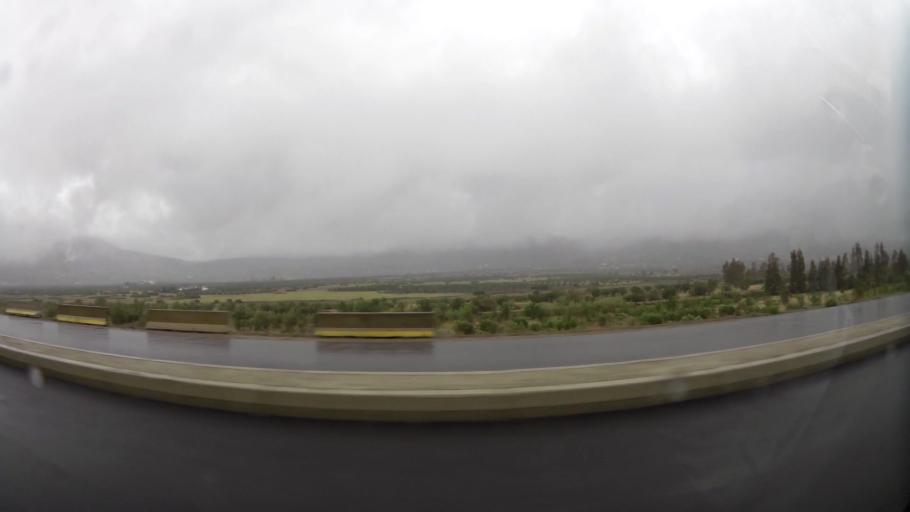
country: MA
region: Oriental
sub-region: Nador
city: Midar
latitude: 34.8274
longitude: -3.7203
